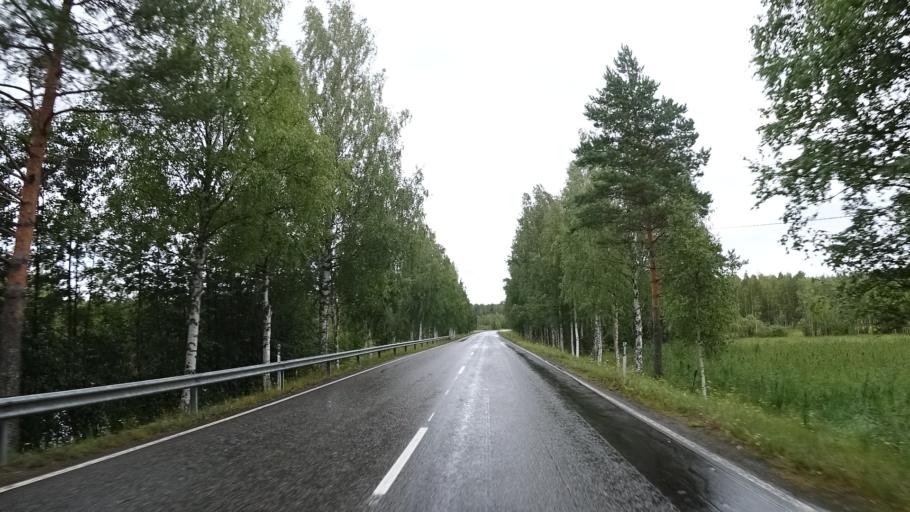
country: FI
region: Southern Savonia
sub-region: Savonlinna
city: Kerimaeki
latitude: 62.0335
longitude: 29.5175
